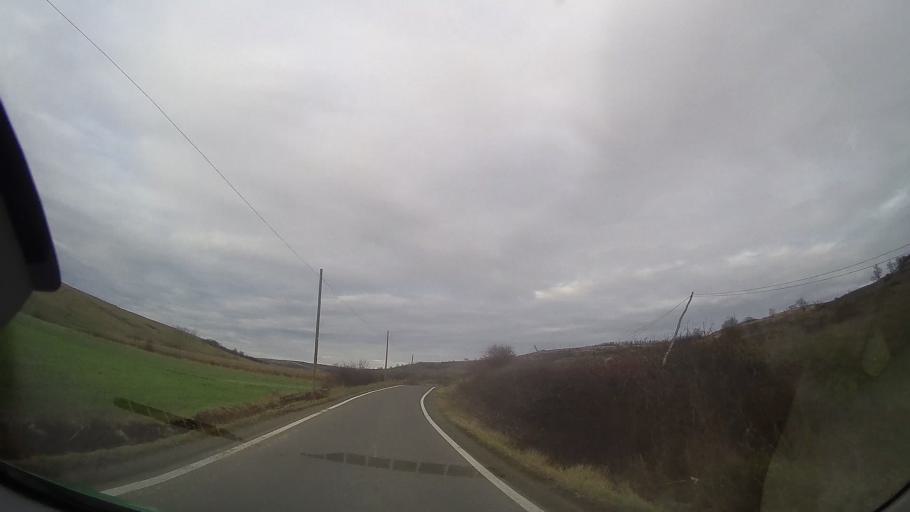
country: RO
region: Mures
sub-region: Comuna Cozma
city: Cozma
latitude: 46.7984
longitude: 24.5383
